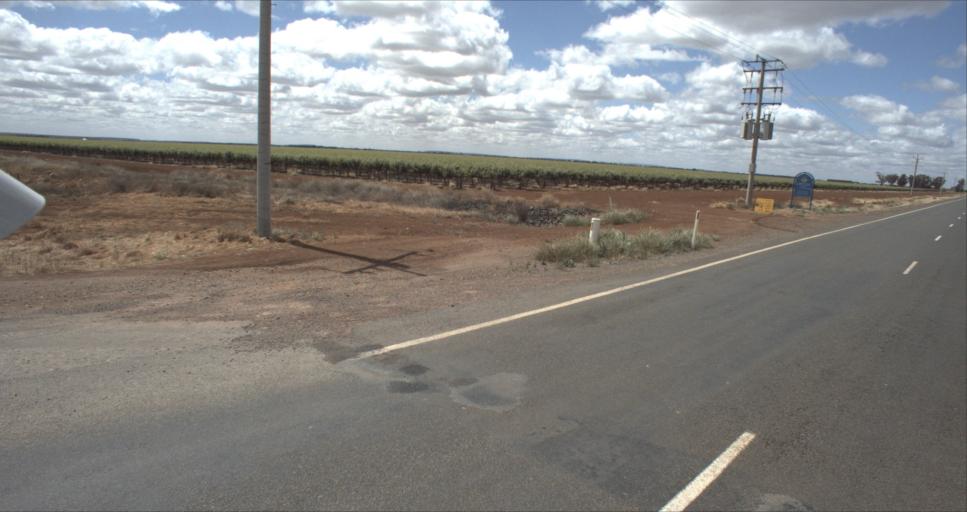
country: AU
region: New South Wales
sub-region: Murrumbidgee Shire
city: Darlington Point
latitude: -34.4690
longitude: 146.1365
